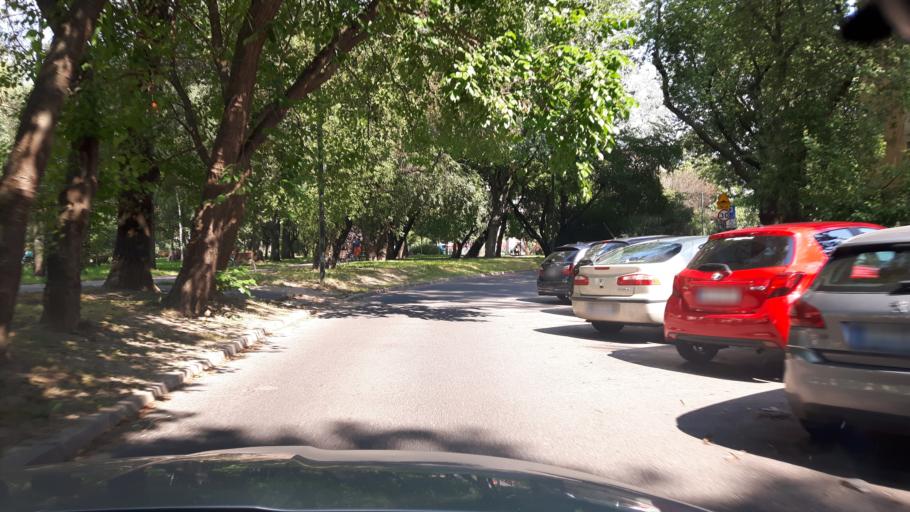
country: PL
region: Masovian Voivodeship
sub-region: Warszawa
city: Ochota
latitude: 52.2103
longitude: 20.9724
